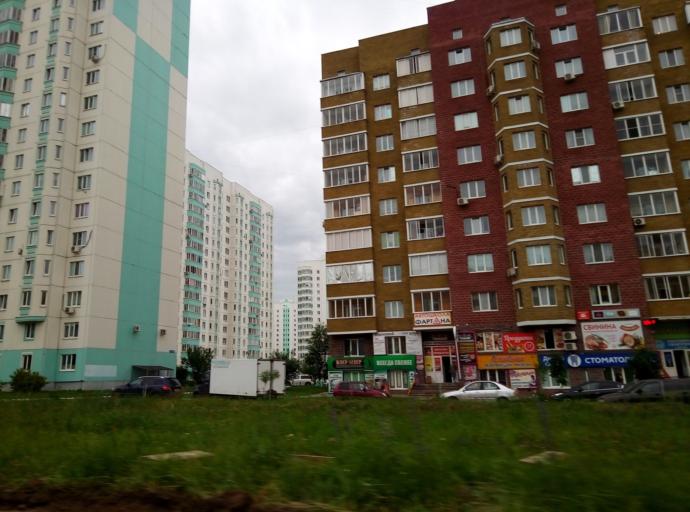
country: RU
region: Kursk
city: Kursk
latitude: 51.7243
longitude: 36.1378
